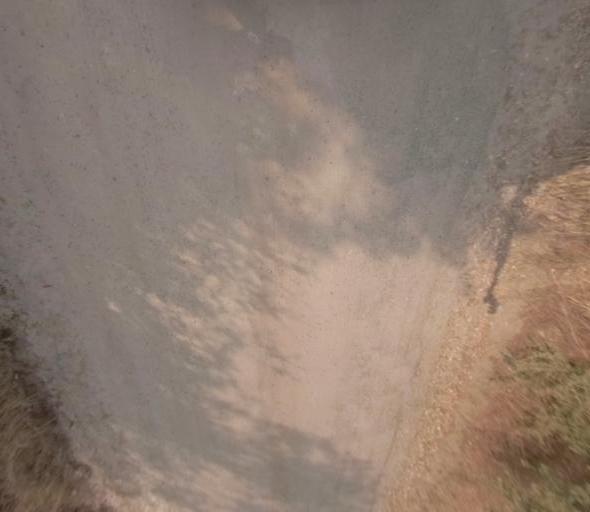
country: US
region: California
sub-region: Madera County
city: Coarsegold
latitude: 37.1961
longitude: -119.6879
